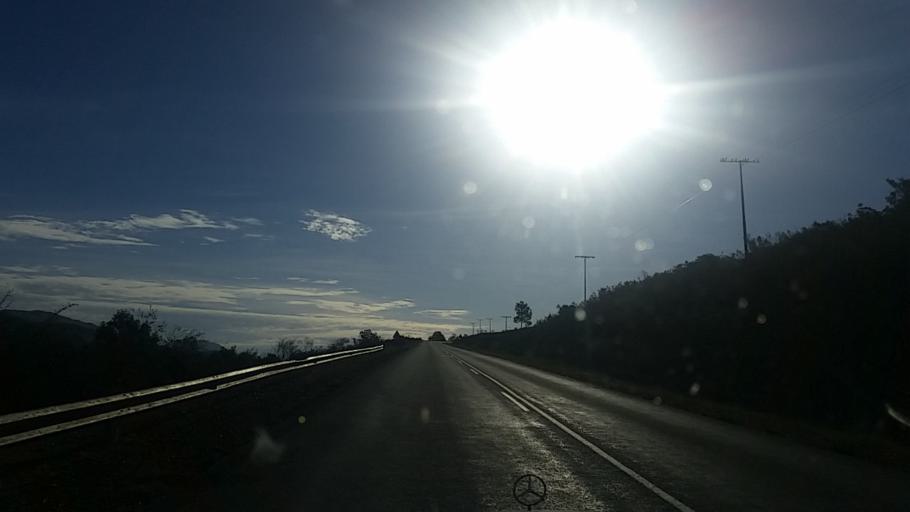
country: ZA
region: Western Cape
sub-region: Eden District Municipality
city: Knysna
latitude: -33.7600
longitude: 22.9585
